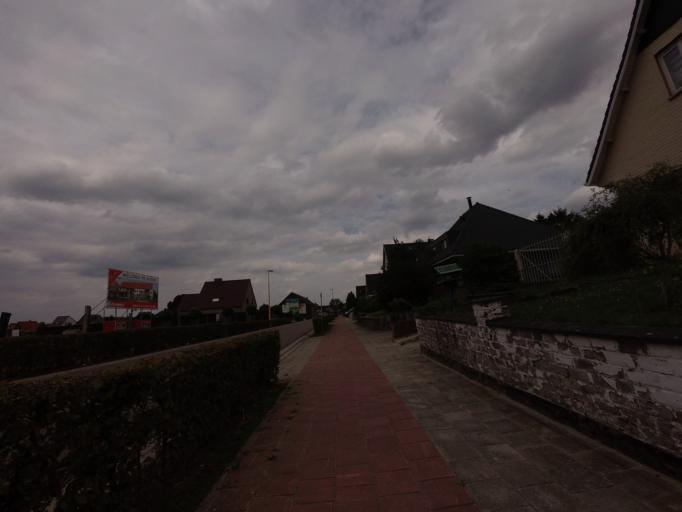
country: BE
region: Flanders
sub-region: Provincie Vlaams-Brabant
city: Grimbergen
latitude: 50.9274
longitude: 4.3782
